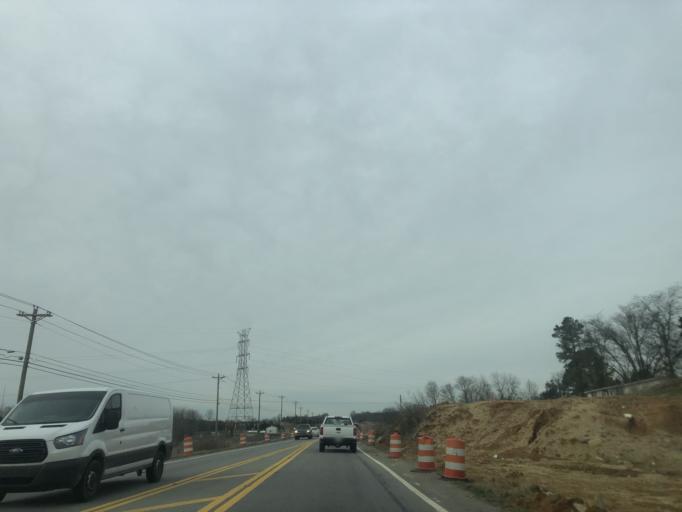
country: US
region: Tennessee
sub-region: Wilson County
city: Mount Juliet
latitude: 36.2453
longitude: -86.4336
